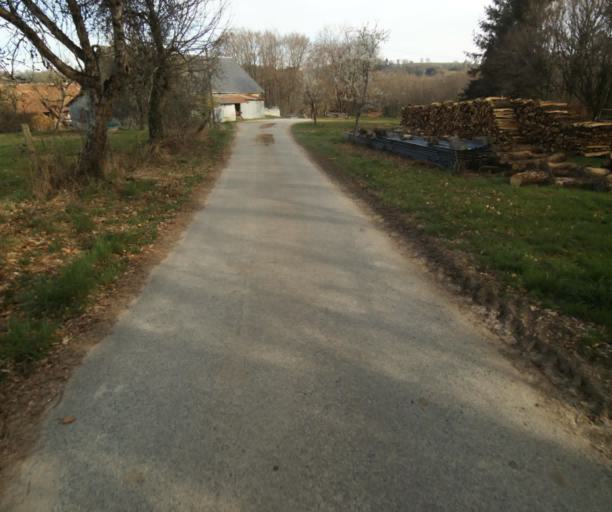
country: FR
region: Limousin
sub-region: Departement de la Correze
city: Chamboulive
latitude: 45.4414
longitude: 1.7453
